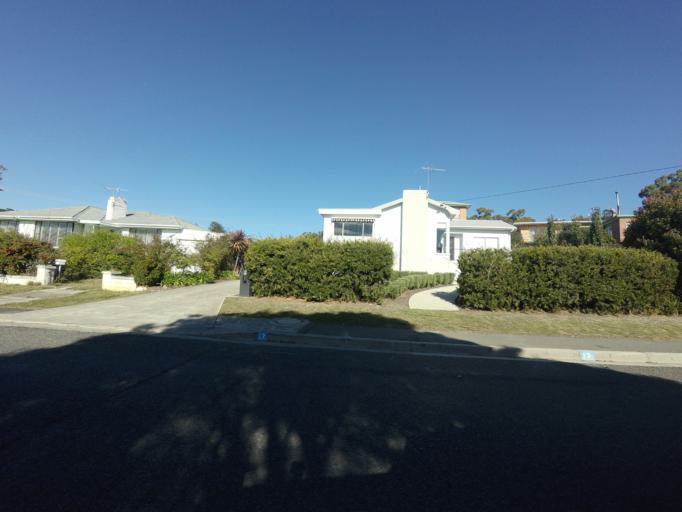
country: AU
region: Tasmania
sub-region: Clarence
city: Lindisfarne
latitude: -42.8399
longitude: 147.3502
